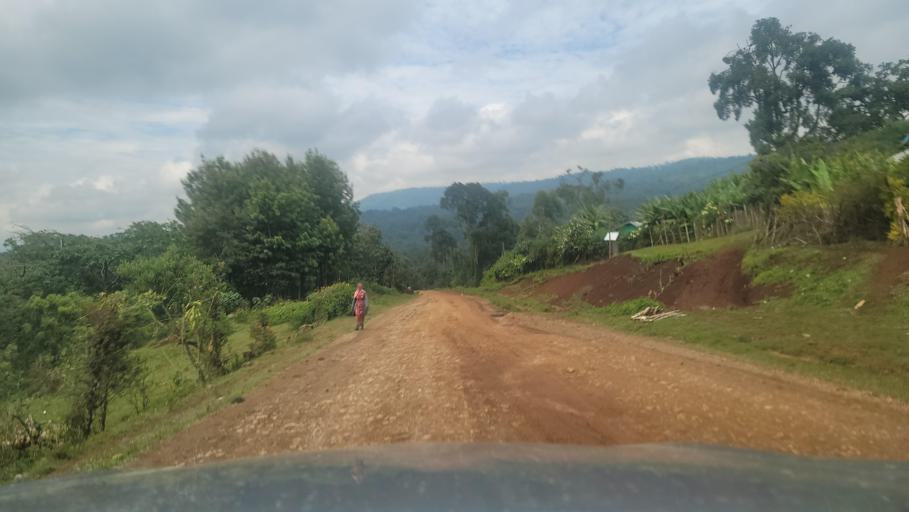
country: ET
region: Oromiya
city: Agaro
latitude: 7.7920
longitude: 36.4391
